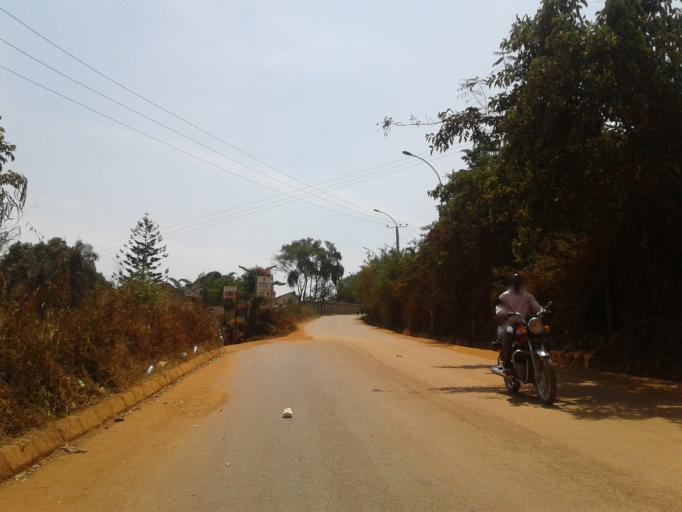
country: UG
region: Central Region
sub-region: Kampala District
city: Kampala
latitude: 0.2655
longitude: 32.6284
